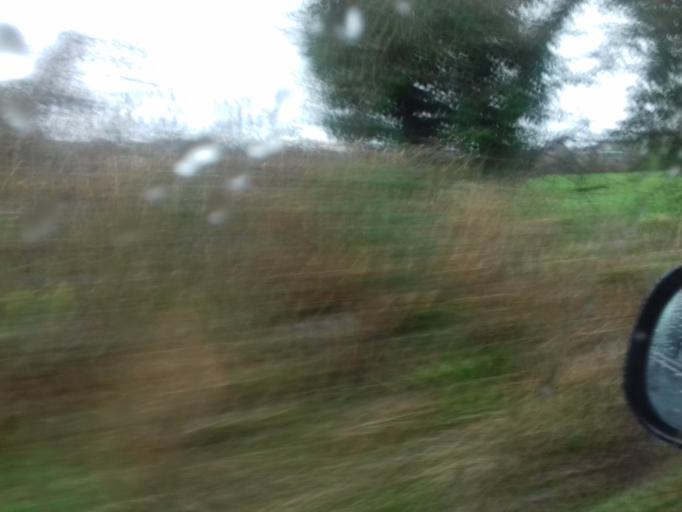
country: IE
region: Leinster
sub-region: Kilkenny
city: Graiguenamanagh
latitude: 52.5915
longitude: -6.9982
